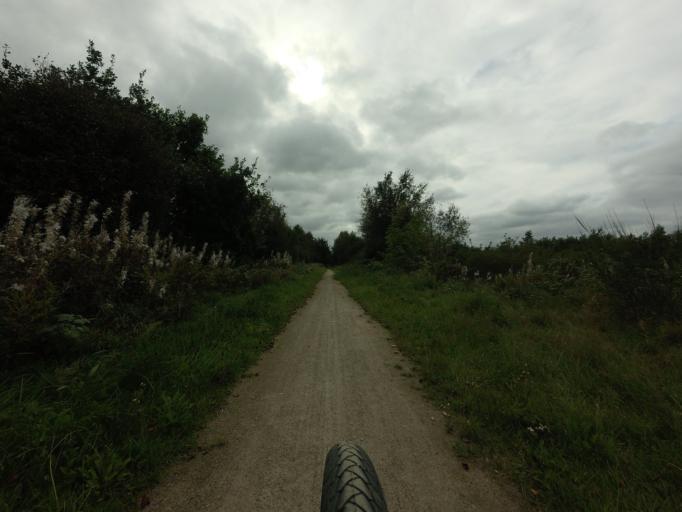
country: DK
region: South Denmark
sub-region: Billund Kommune
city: Billund
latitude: 55.8075
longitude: 9.0212
